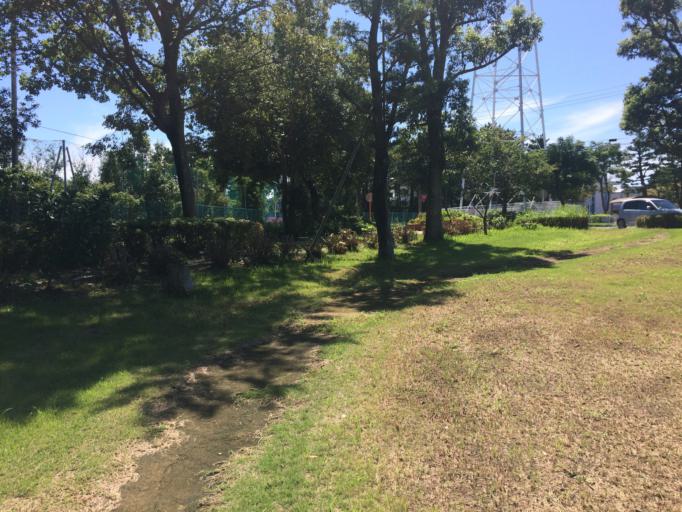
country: JP
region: Shizuoka
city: Shizuoka-shi
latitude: 34.9885
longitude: 138.5127
